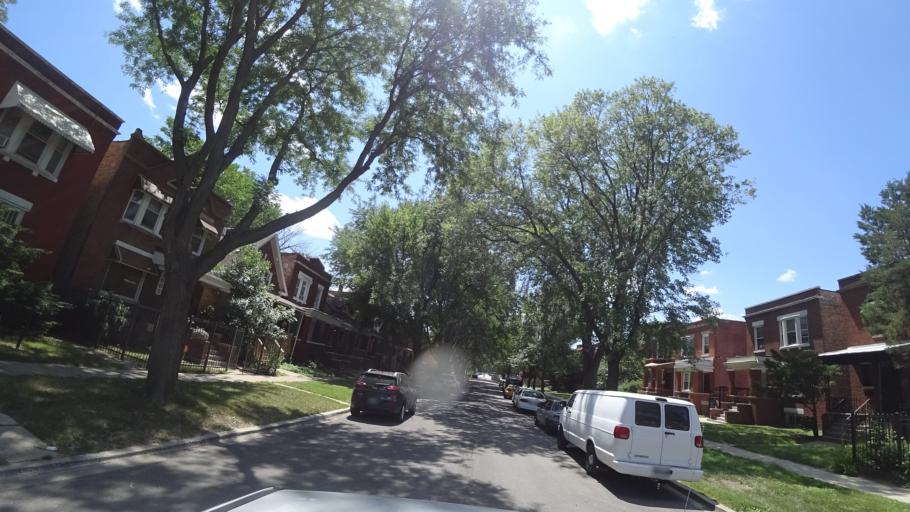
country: US
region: Illinois
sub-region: Cook County
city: Chicago
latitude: 41.7675
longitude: -87.6169
